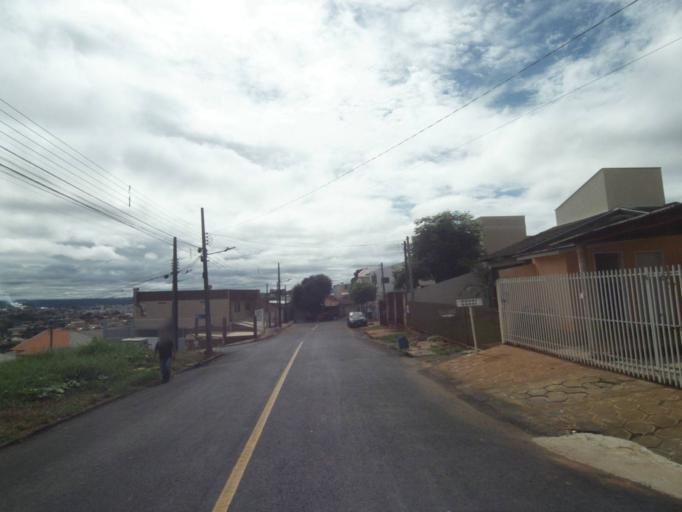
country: BR
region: Parana
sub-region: Telemaco Borba
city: Telemaco Borba
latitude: -24.3339
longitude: -50.6419
